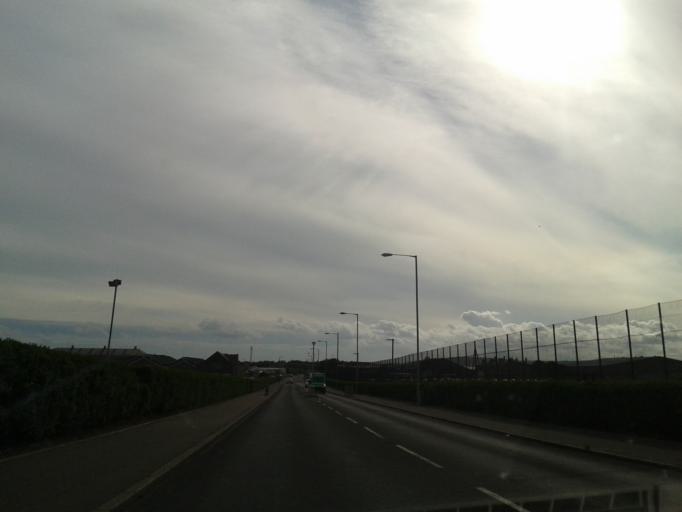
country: GB
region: Scotland
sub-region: Aberdeenshire
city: Fraserburgh
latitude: 57.6856
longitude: -2.0058
